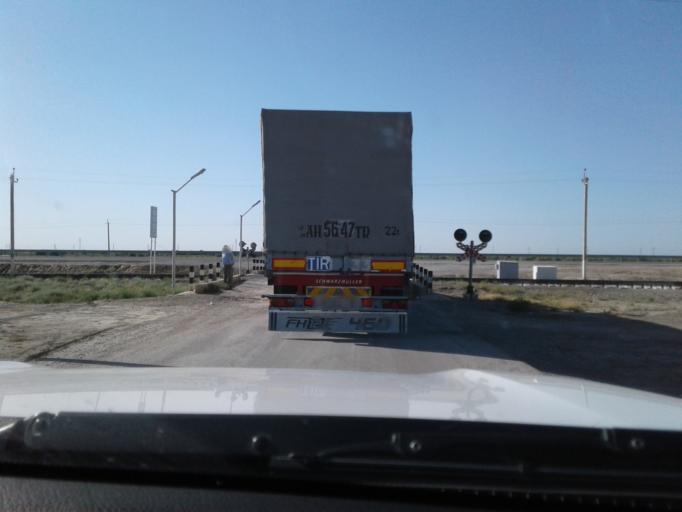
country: IR
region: Razavi Khorasan
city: Kalat-e Naderi
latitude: 37.2026
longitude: 60.0424
